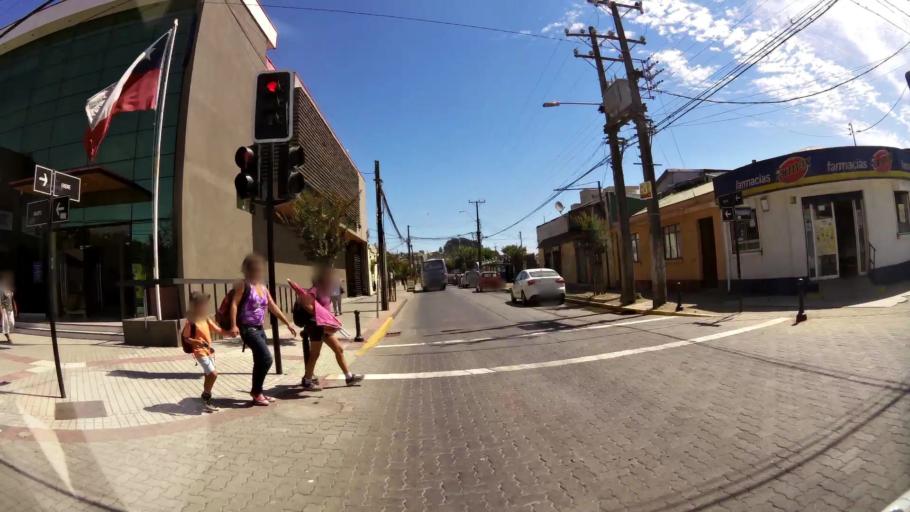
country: CL
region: Biobio
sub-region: Provincia de Concepcion
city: Penco
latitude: -36.7368
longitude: -72.9940
